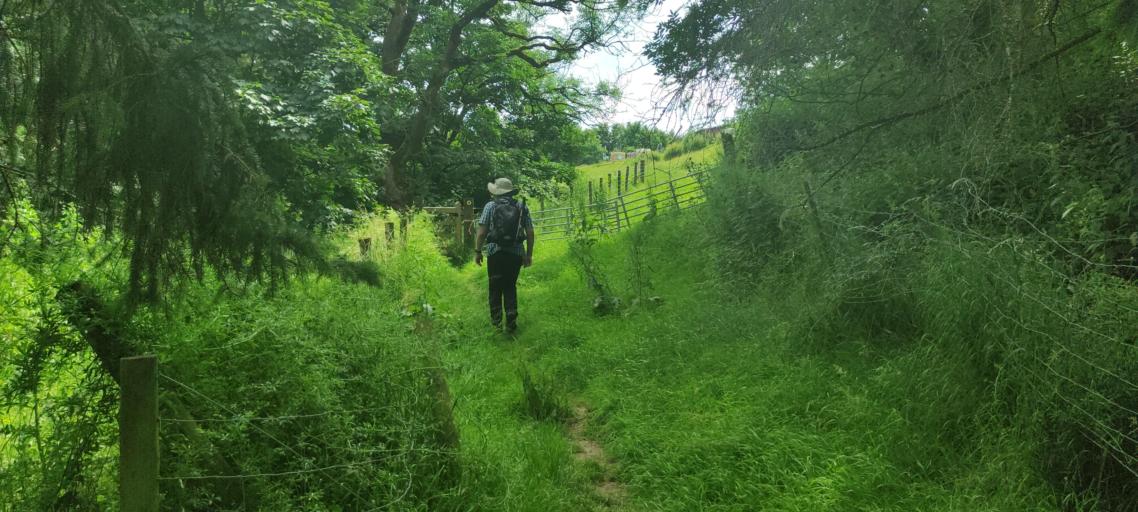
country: GB
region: England
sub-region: Cumbria
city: Kirkby Stephen
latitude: 54.4369
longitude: -2.4337
